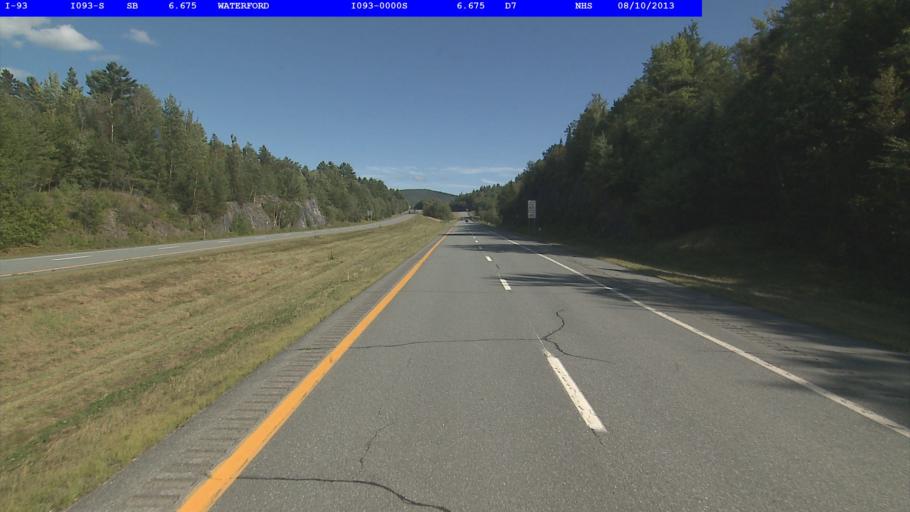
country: US
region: Vermont
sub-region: Caledonia County
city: St Johnsbury
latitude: 44.4258
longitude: -71.9407
